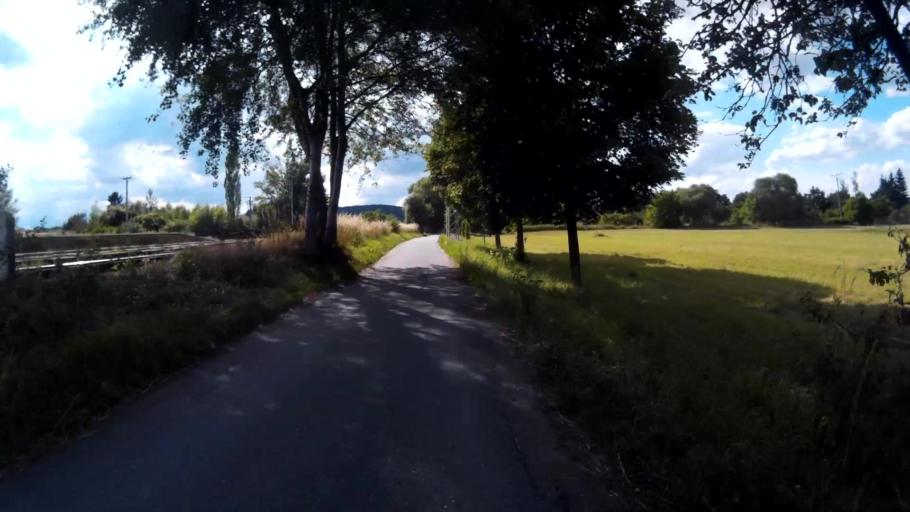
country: CZ
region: South Moravian
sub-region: Okres Brno-Venkov
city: Rosice
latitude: 49.1727
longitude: 16.4074
